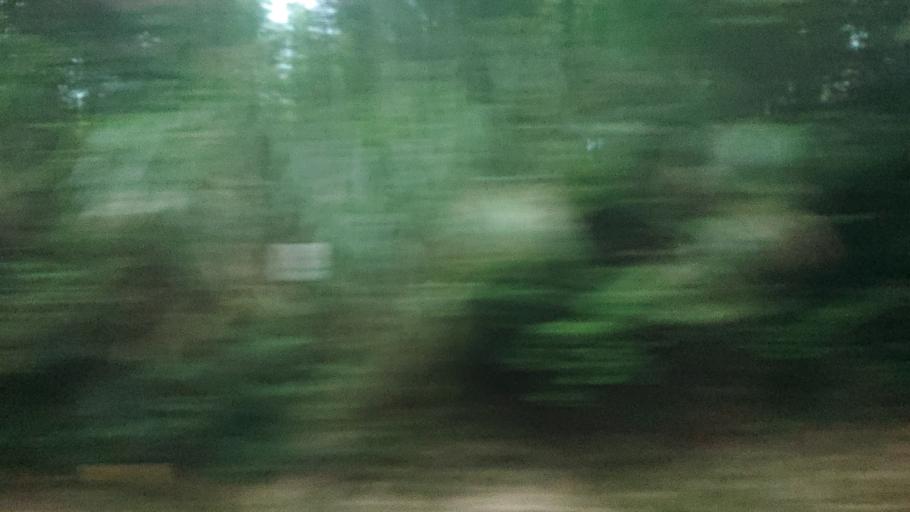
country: TW
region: Taiwan
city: Lugu
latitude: 23.5150
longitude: 120.6990
